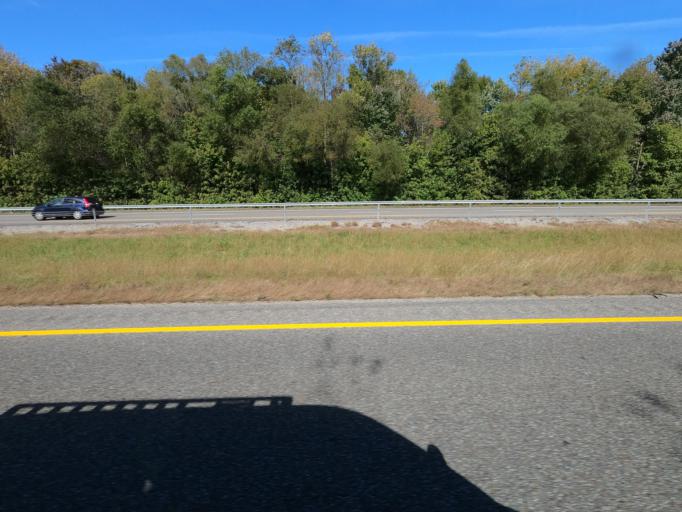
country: US
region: Tennessee
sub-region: Madison County
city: Jackson
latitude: 35.6516
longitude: -88.8875
